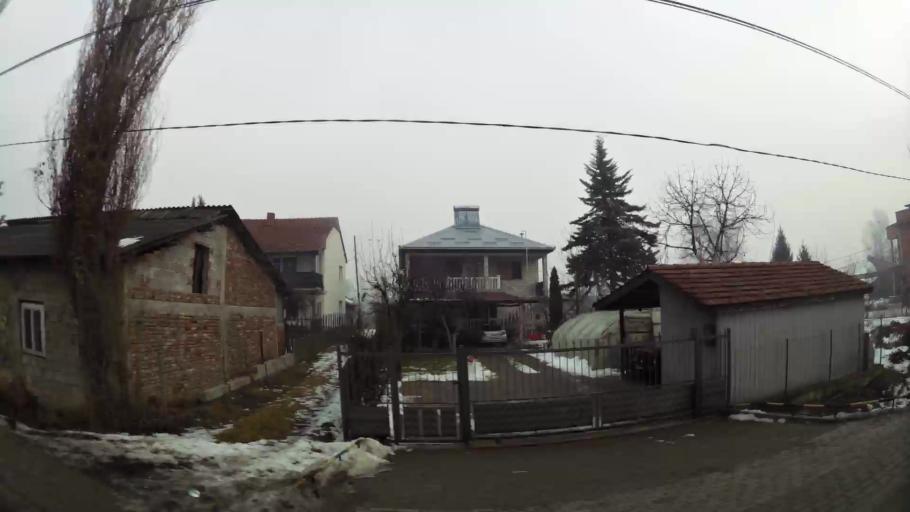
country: MK
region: Ilinden
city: Idrizovo
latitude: 41.9556
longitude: 21.5744
